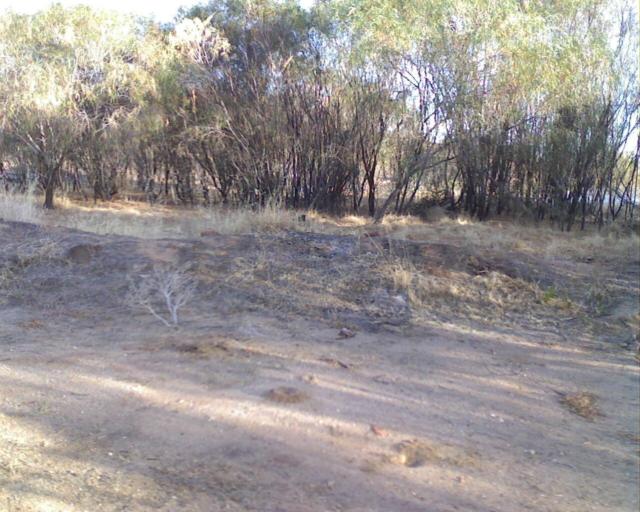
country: AU
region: Western Australia
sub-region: Merredin
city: Merredin
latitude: -30.9477
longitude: 117.8587
